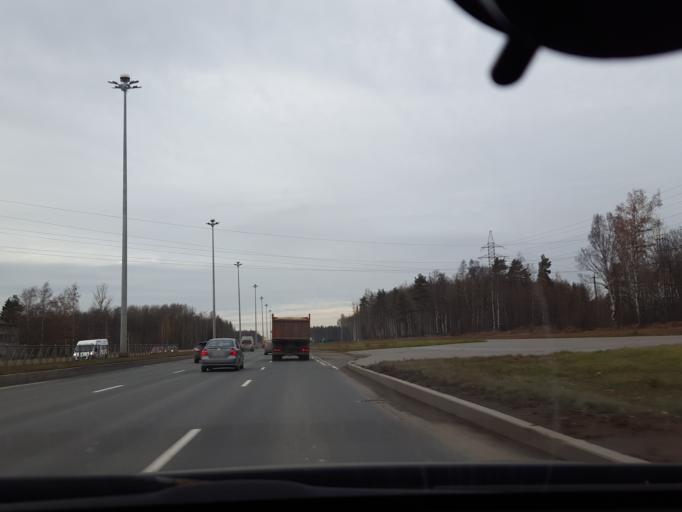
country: RU
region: Leningrad
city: Untolovo
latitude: 60.0448
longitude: 30.2365
